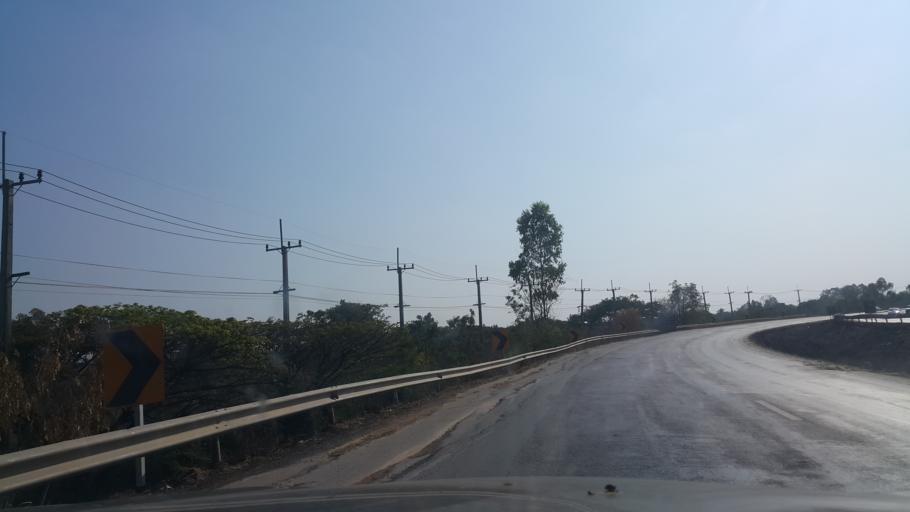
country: TH
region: Khon Kaen
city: Khon Kaen
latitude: 16.4202
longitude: 102.9168
